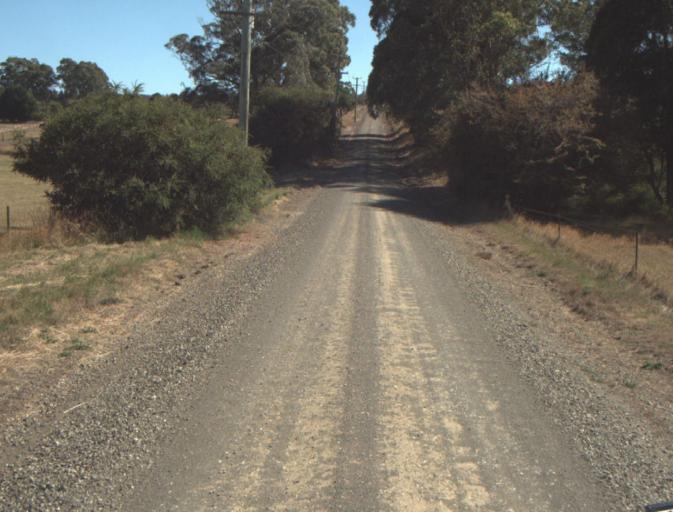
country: AU
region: Tasmania
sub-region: Launceston
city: Newstead
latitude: -41.3154
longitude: 147.3204
